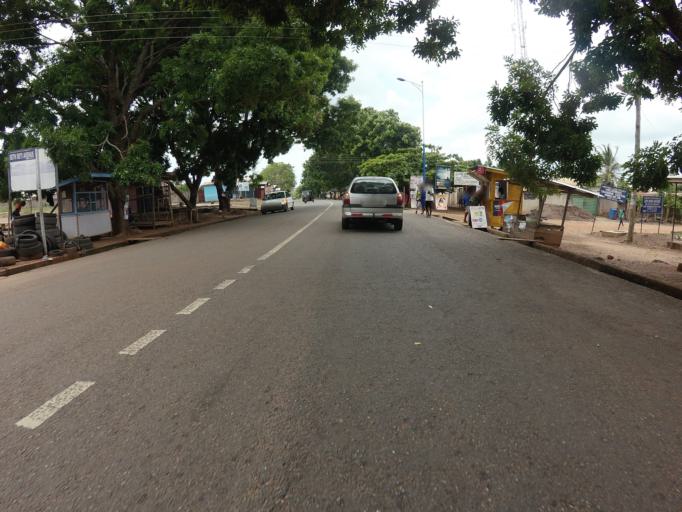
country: GH
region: Volta
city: Ho
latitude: 6.6163
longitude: 0.4927
